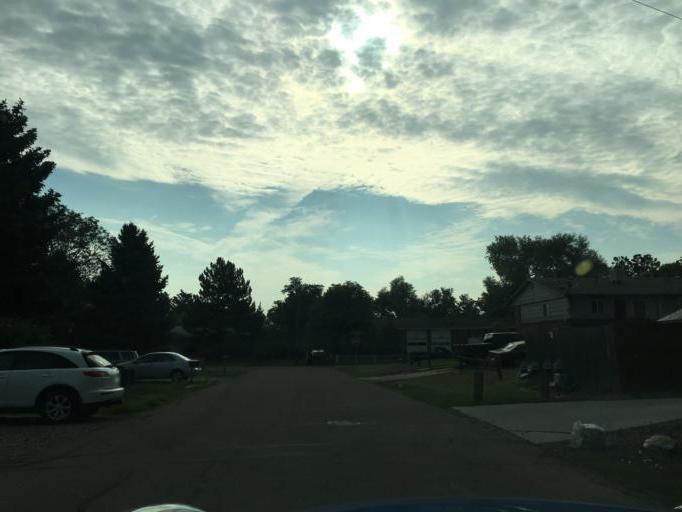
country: US
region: Colorado
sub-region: Jefferson County
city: Wheat Ridge
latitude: 39.7438
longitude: -105.1057
